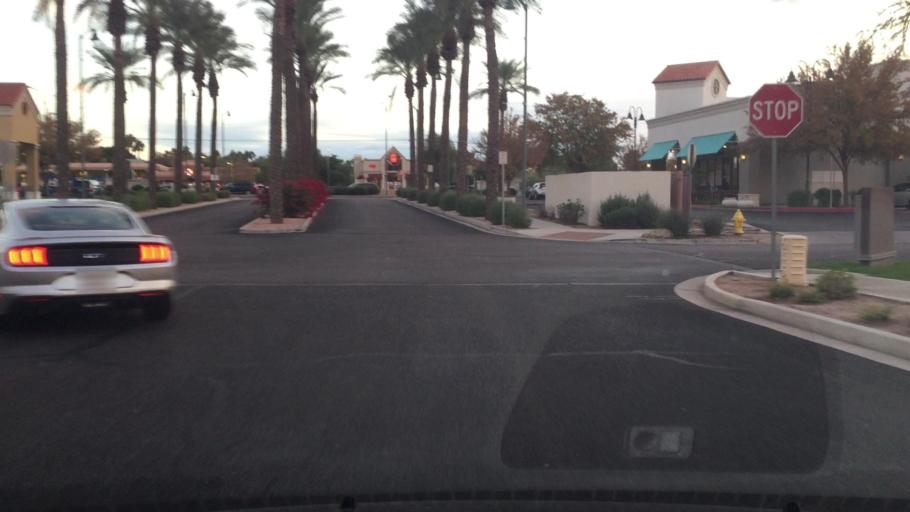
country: US
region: Arizona
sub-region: Maricopa County
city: Gilbert
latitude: 33.3802
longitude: -111.7551
